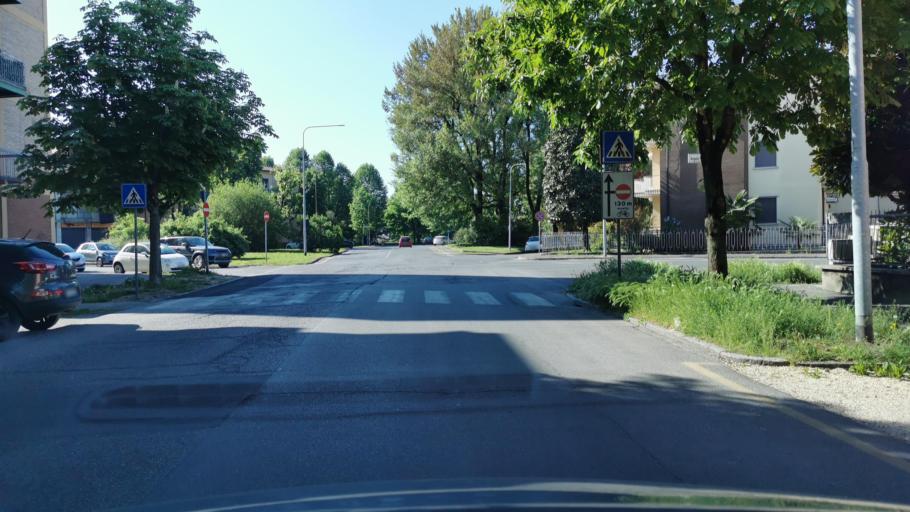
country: IT
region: Lombardy
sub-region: Provincia di Cremona
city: Cremona
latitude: 45.1325
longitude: 10.0376
